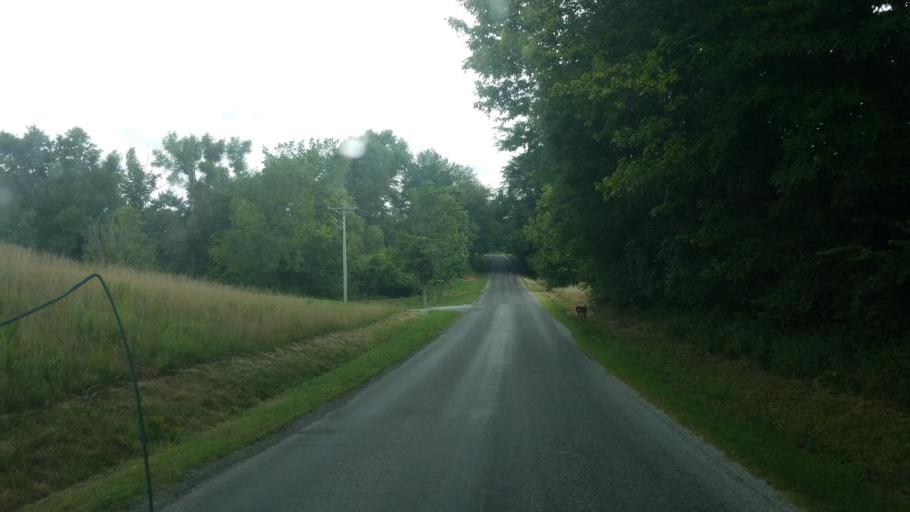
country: US
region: Illinois
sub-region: Jackson County
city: Murphysboro
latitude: 37.7031
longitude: -89.3333
